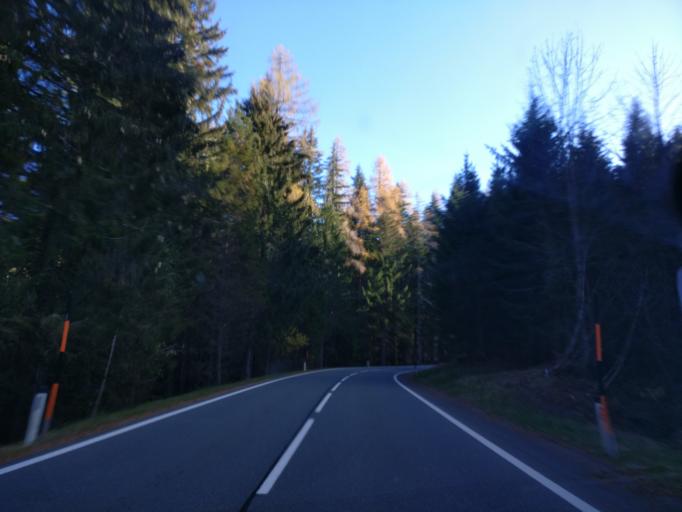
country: AT
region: Salzburg
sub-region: Politischer Bezirk Zell am See
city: Dienten am Hochkonig
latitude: 47.4056
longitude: 12.9842
